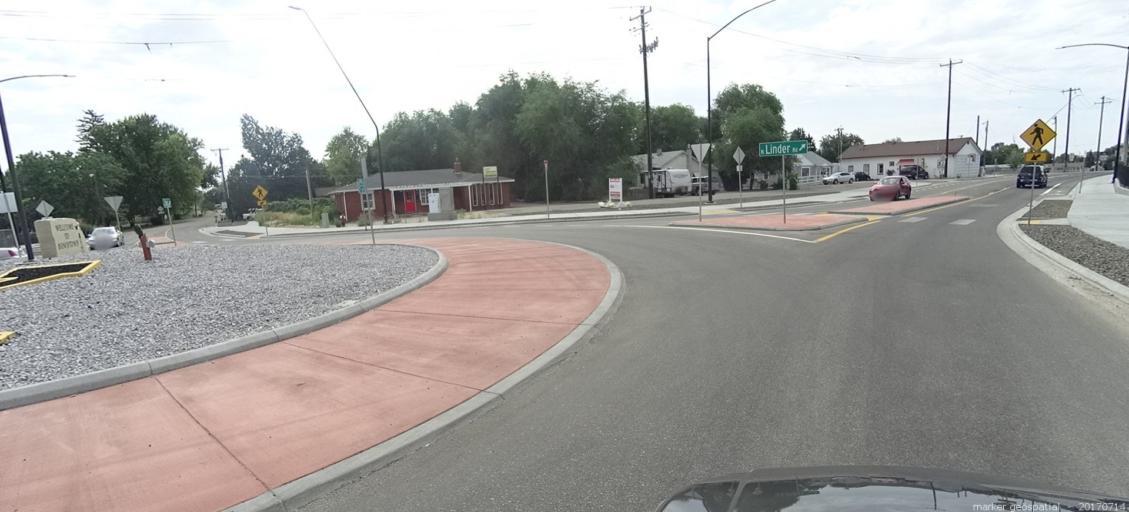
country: US
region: Idaho
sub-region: Ada County
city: Kuna
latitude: 43.4905
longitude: -116.4141
